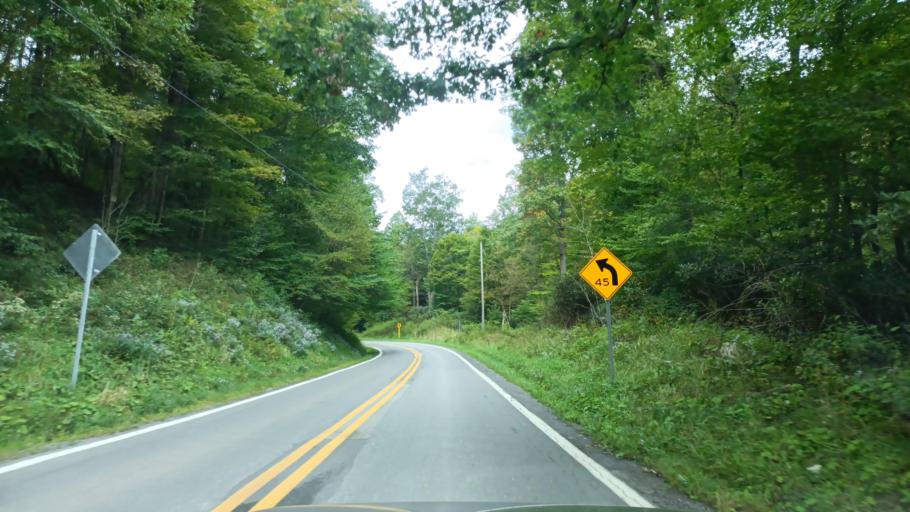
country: US
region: West Virginia
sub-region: Preston County
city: Kingwood
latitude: 39.3213
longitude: -79.7157
